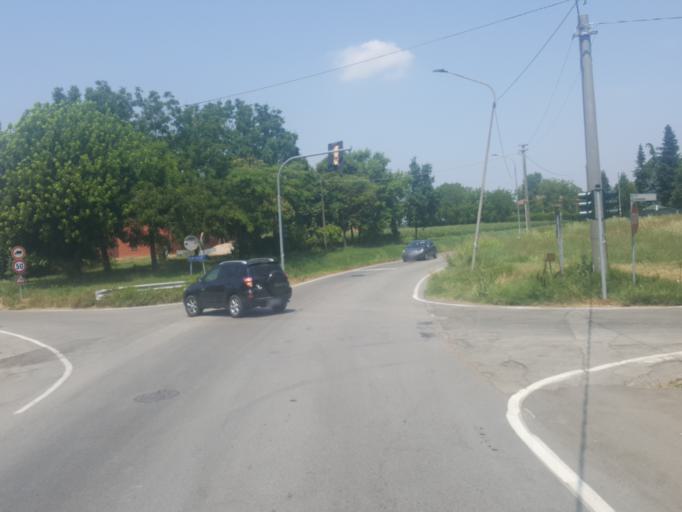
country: IT
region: Emilia-Romagna
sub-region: Provincia di Modena
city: Manzolino
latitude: 44.6099
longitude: 11.0847
